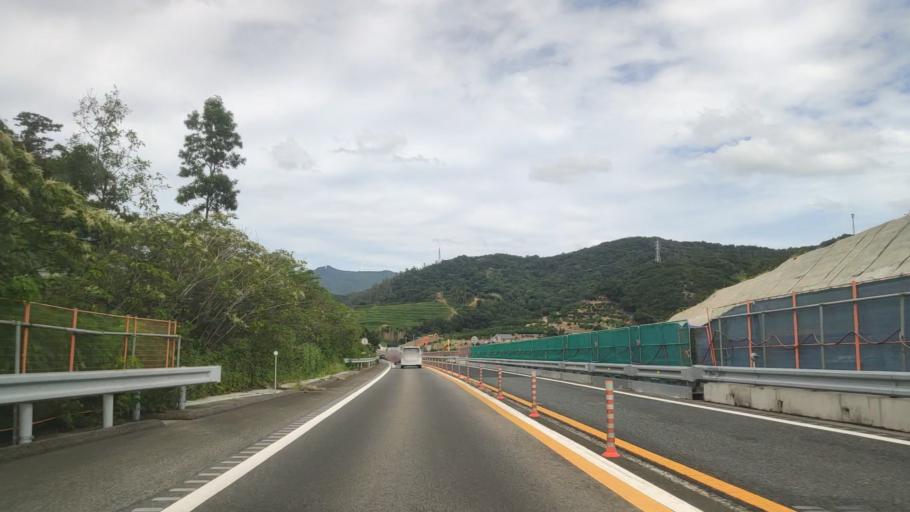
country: JP
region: Wakayama
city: Gobo
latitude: 33.9117
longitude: 135.1944
